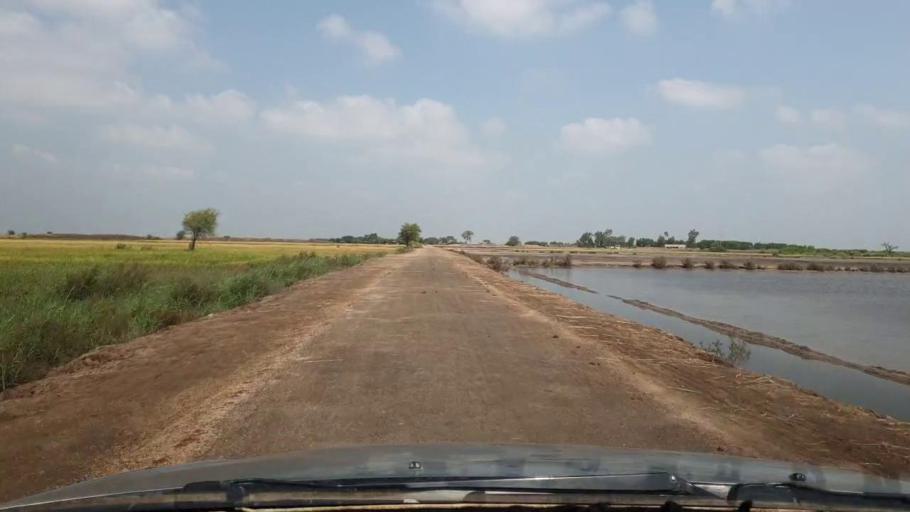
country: PK
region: Sindh
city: Matli
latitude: 25.0901
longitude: 68.6915
